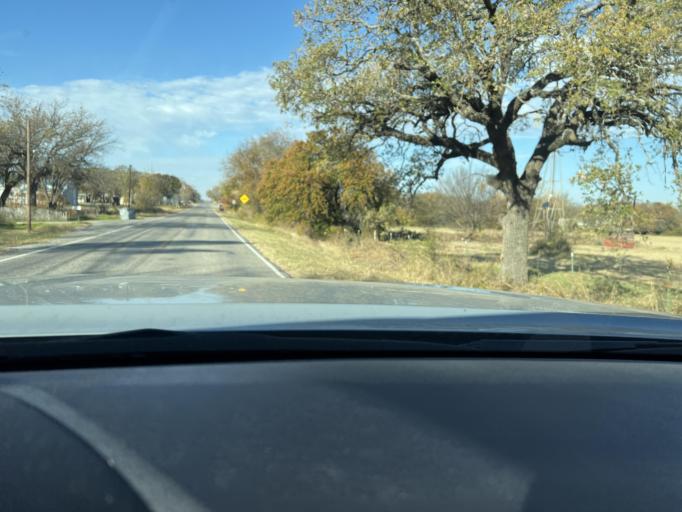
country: US
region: Texas
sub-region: Eastland County
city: Eastland
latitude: 32.4193
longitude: -98.7482
